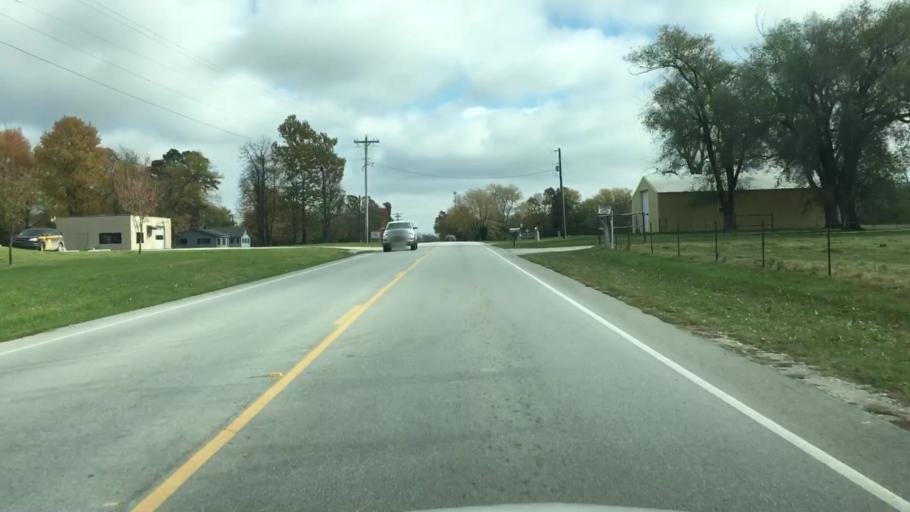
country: US
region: Arkansas
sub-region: Benton County
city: Centerton
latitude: 36.2616
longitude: -94.3590
